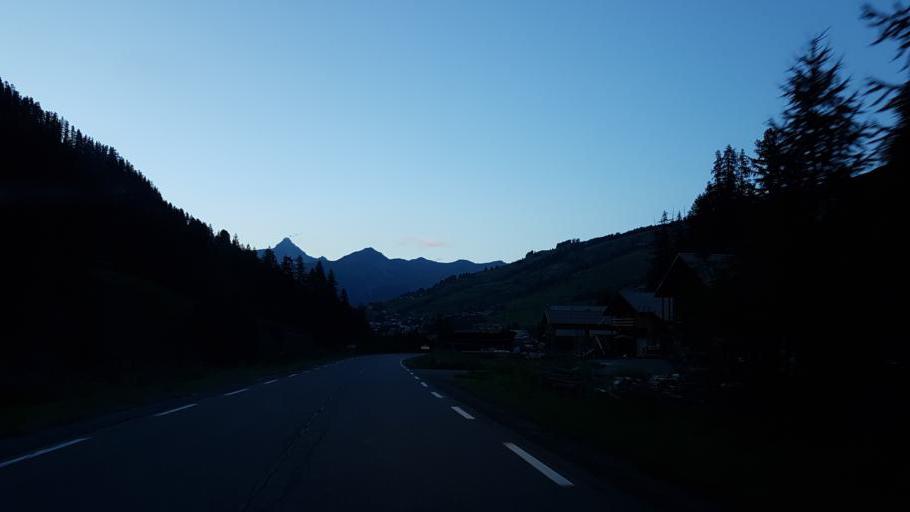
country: IT
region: Piedmont
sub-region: Provincia di Cuneo
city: Pontechianale
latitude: 44.7151
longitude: 6.8481
